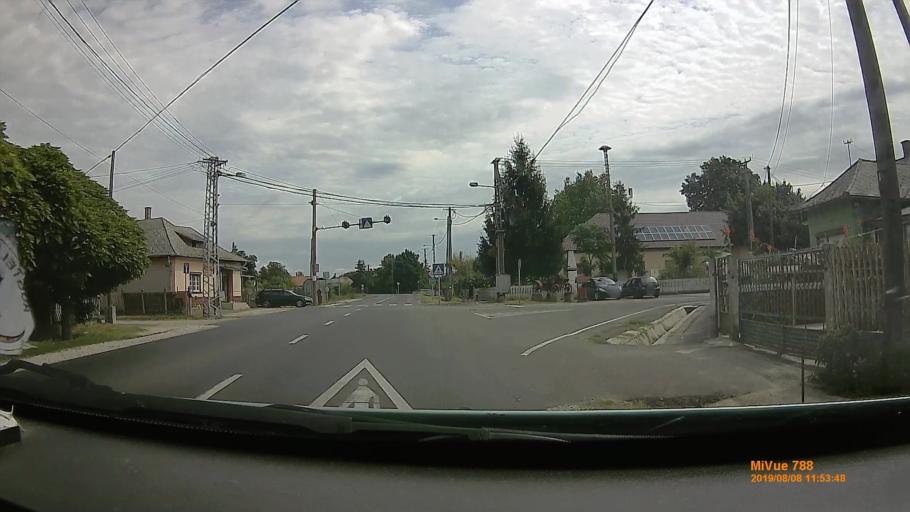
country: HU
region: Szabolcs-Szatmar-Bereg
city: Nyirmihalydi
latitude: 47.7333
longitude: 21.9638
